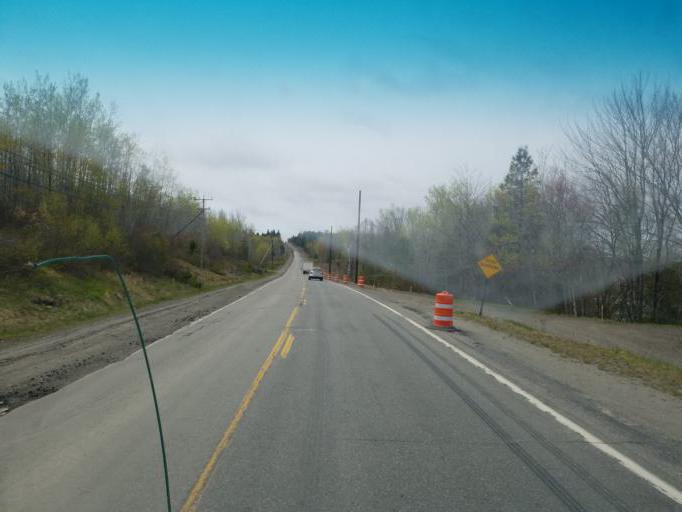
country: US
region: Maine
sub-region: Washington County
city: East Machias
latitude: 44.7798
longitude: -67.1950
